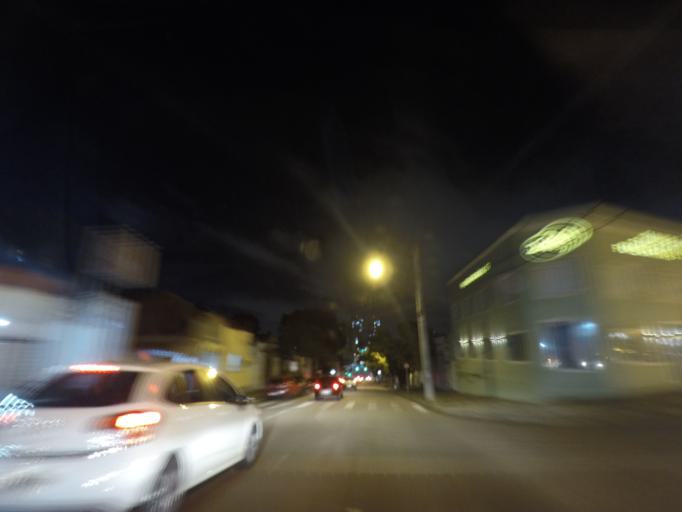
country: BR
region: Parana
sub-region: Curitiba
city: Curitiba
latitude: -25.4218
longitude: -49.2745
